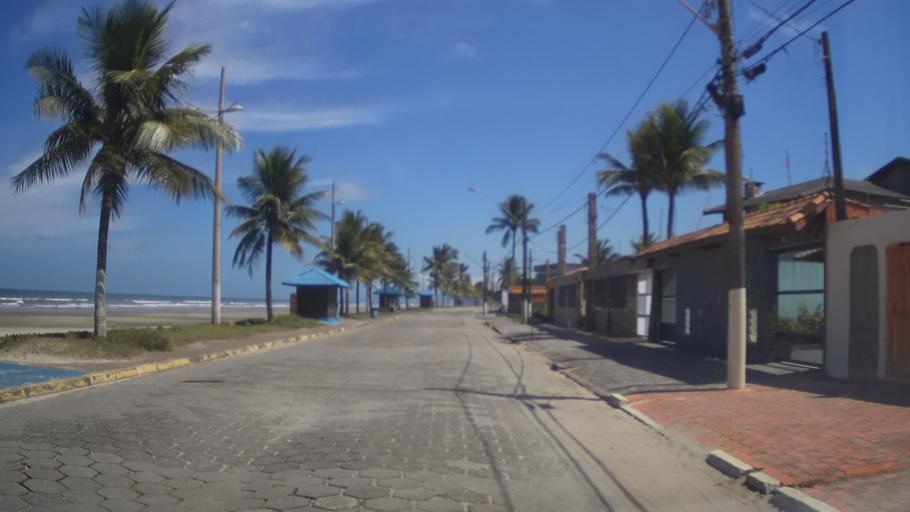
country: BR
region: Sao Paulo
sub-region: Mongagua
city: Mongagua
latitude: -24.1389
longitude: -46.7028
